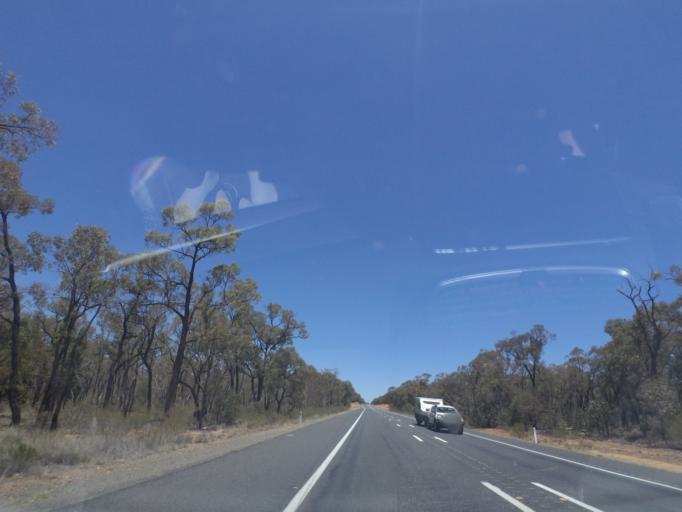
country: AU
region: New South Wales
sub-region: Warrumbungle Shire
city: Coonabarabran
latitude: -30.8915
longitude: 149.4422
